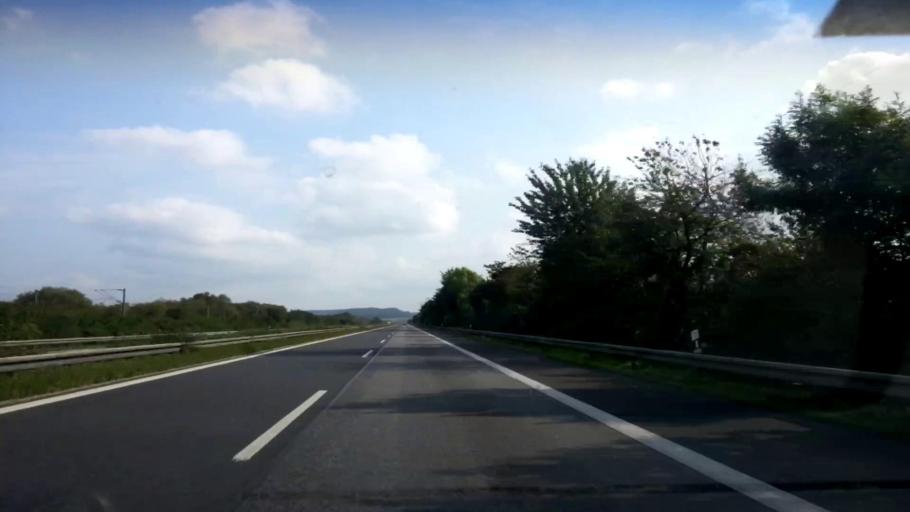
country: DE
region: Bavaria
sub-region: Regierungsbezirk Unterfranken
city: Ebelsbach
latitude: 49.9757
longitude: 10.6906
